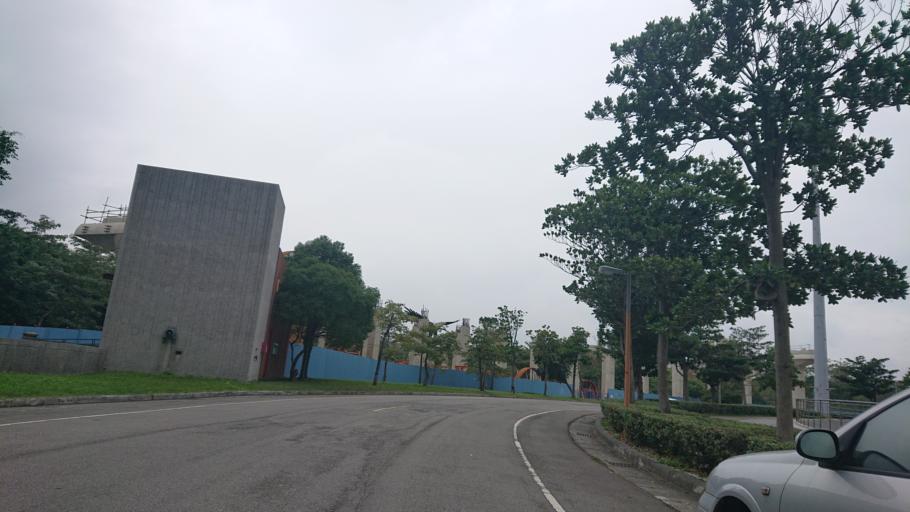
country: TW
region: Taiwan
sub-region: Taoyuan
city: Taoyuan
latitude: 24.9391
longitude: 121.3634
